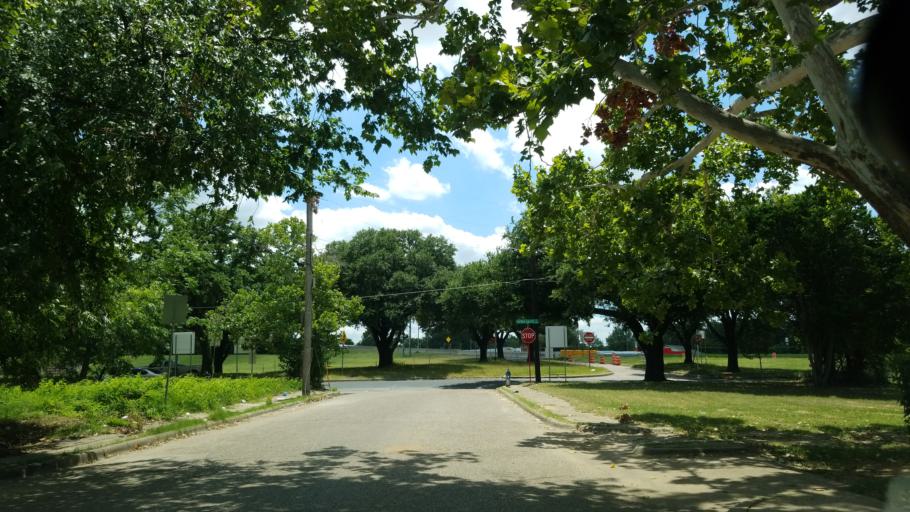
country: US
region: Texas
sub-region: Dallas County
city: Dallas
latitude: 32.7415
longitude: -96.7565
